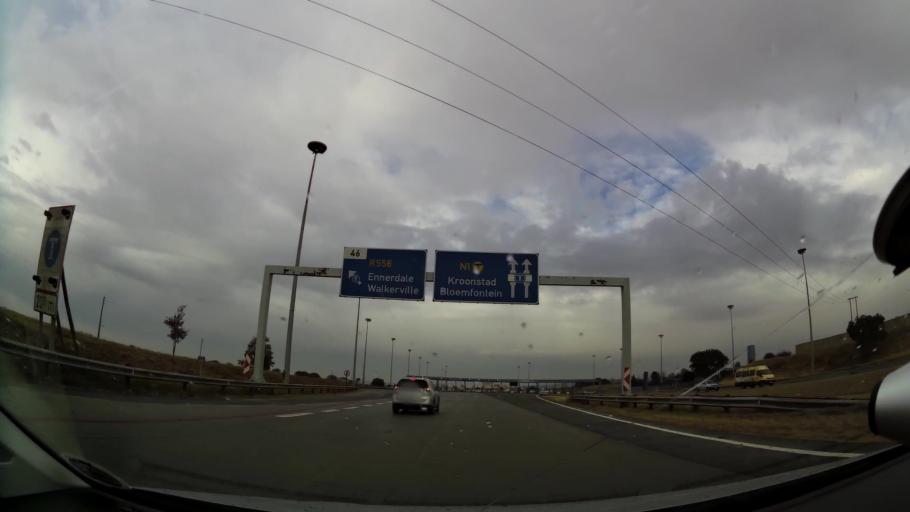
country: ZA
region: Gauteng
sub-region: City of Johannesburg Metropolitan Municipality
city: Orange Farm
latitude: -26.4100
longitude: 27.8854
